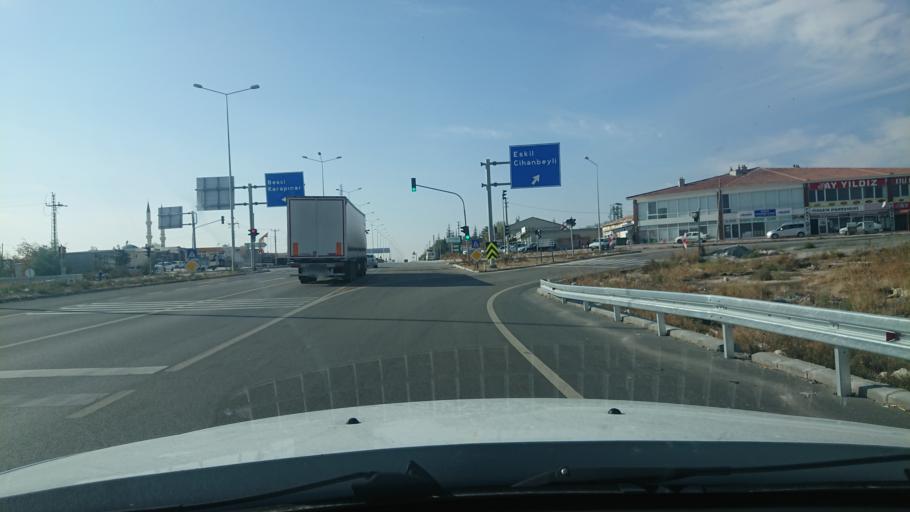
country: TR
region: Aksaray
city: Sultanhani
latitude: 38.2478
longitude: 33.4496
